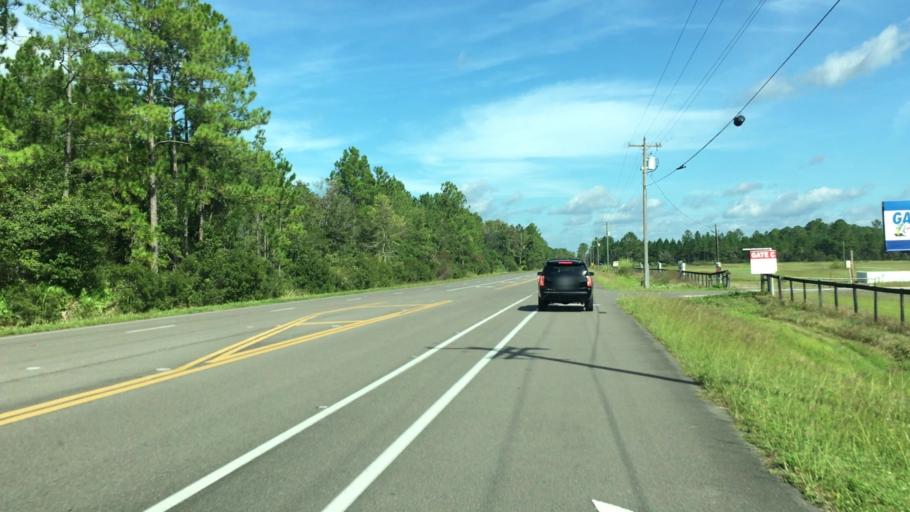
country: US
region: Florida
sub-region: Alachua County
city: Gainesville
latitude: 29.7557
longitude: -82.2783
